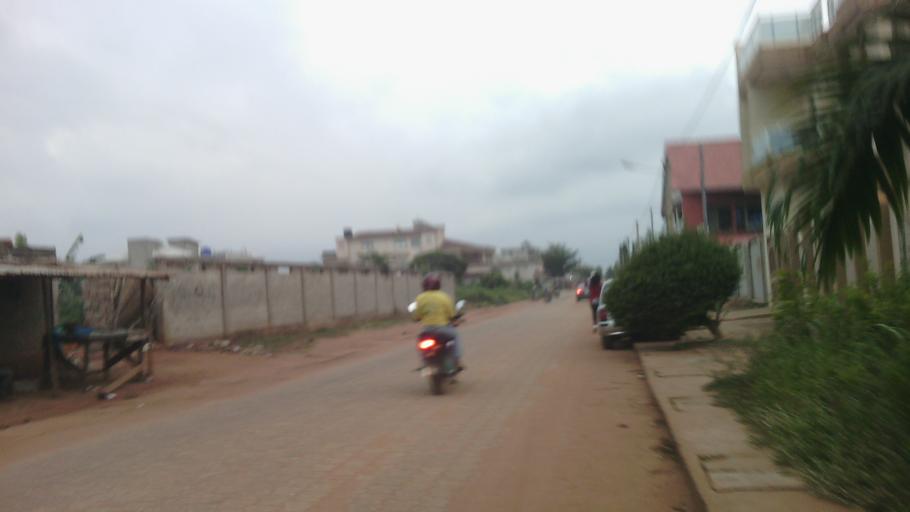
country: BJ
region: Atlantique
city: Abomey-Calavi
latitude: 6.4779
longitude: 2.3479
